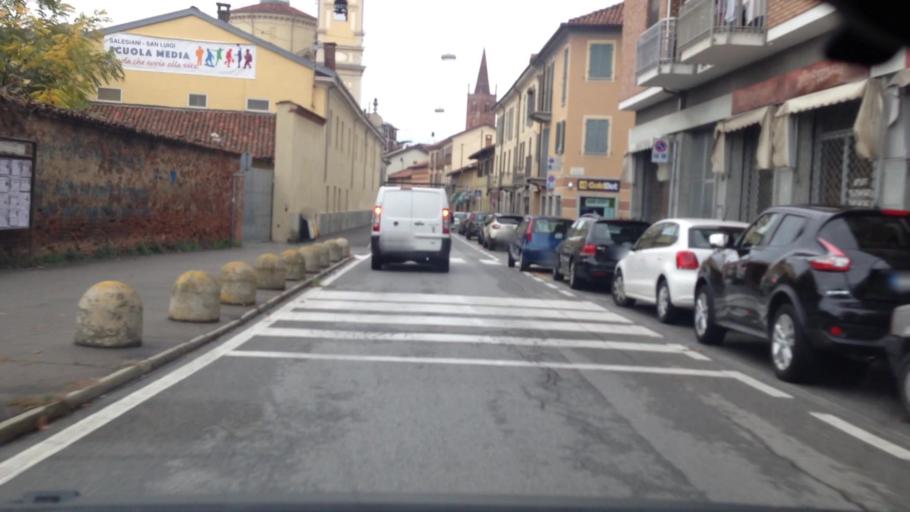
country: IT
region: Piedmont
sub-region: Provincia di Torino
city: Chieri
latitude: 45.0082
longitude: 7.8299
